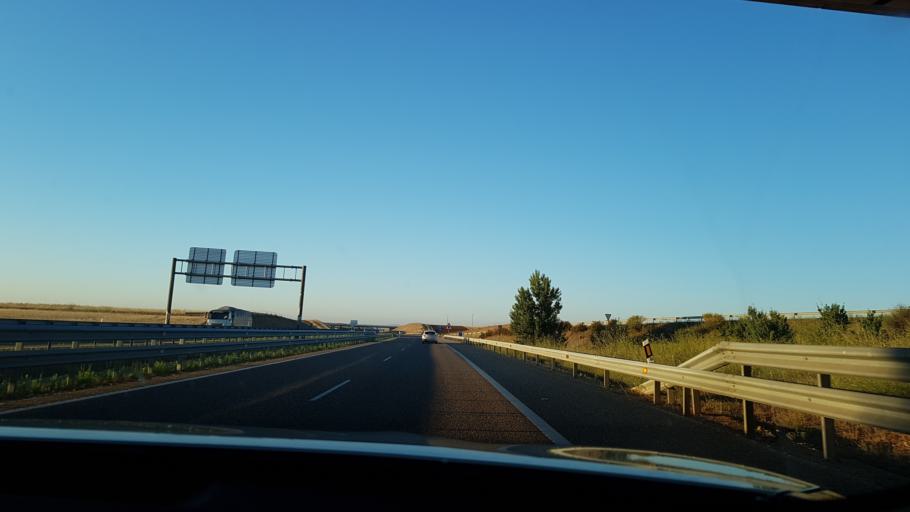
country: ES
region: Castille and Leon
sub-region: Provincia de Zamora
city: Roales
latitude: 41.5776
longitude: -5.7747
